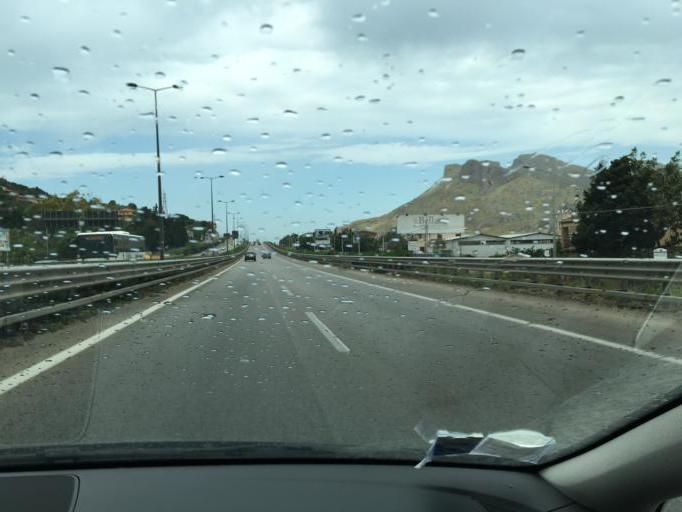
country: IT
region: Sicily
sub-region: Palermo
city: Isola delle Femmine
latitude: 38.1796
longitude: 13.2930
